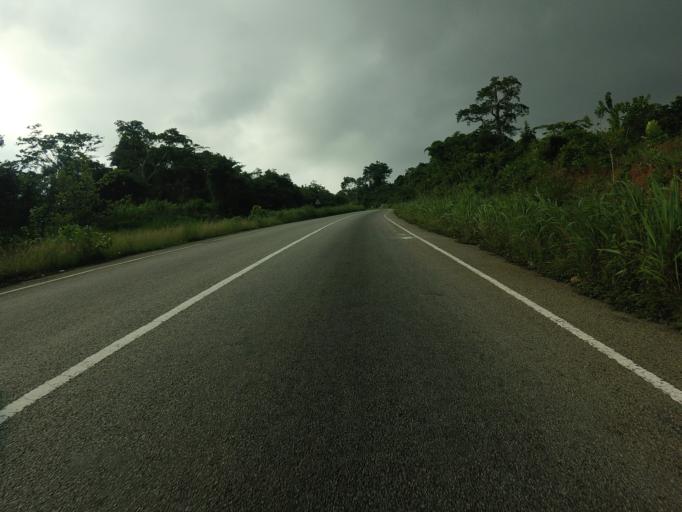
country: GH
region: Volta
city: Ho
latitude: 6.8123
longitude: 0.4206
